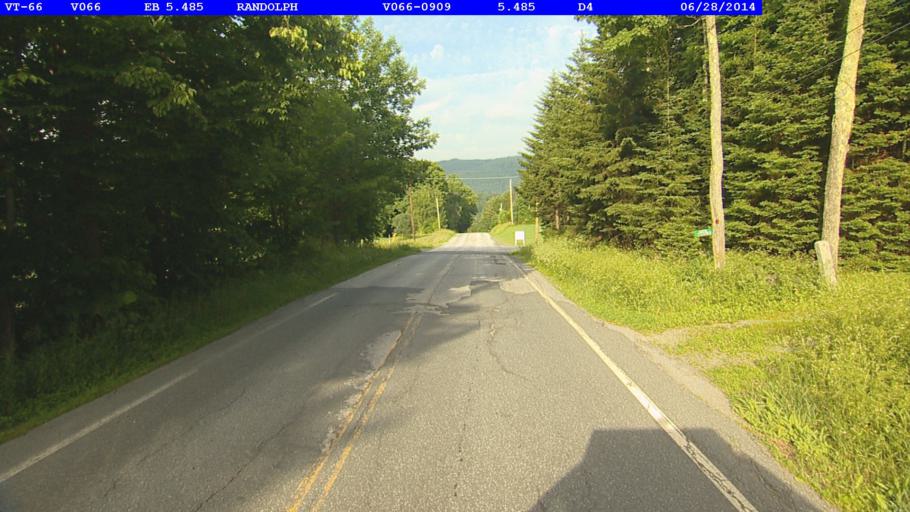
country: US
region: Vermont
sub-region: Orange County
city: Randolph
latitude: 43.9582
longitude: -72.5817
